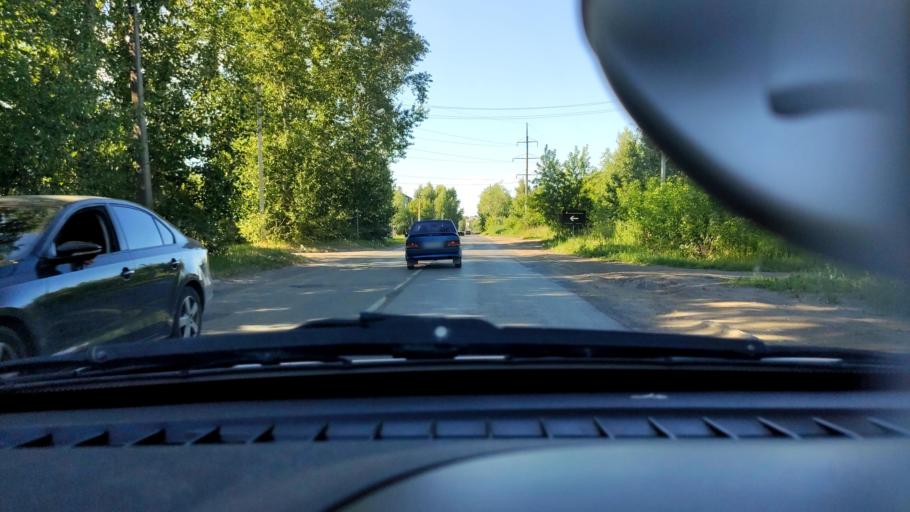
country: RU
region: Perm
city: Krasnokamsk
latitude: 58.0834
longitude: 55.7855
